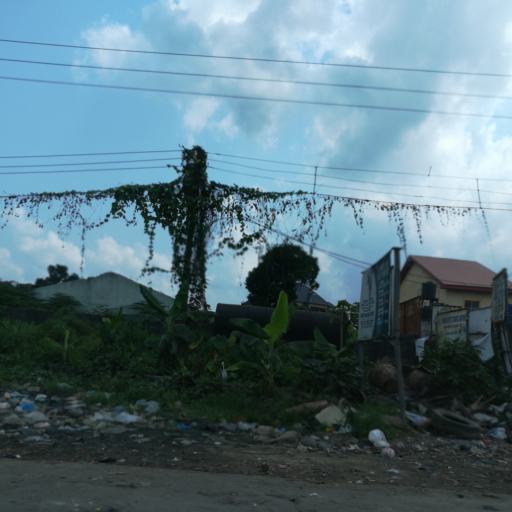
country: NG
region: Rivers
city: Okrika
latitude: 4.8252
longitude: 7.0917
